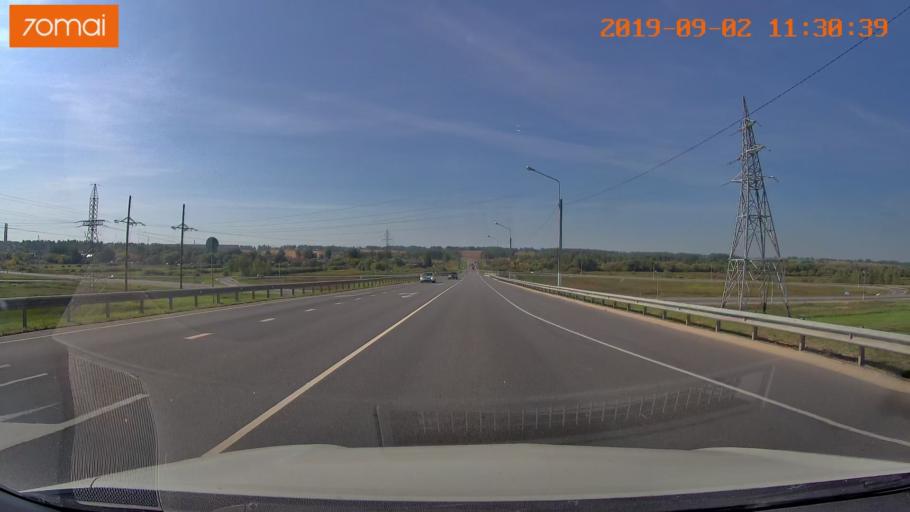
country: RU
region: Smolensk
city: Oster
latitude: 53.9820
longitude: 32.8294
